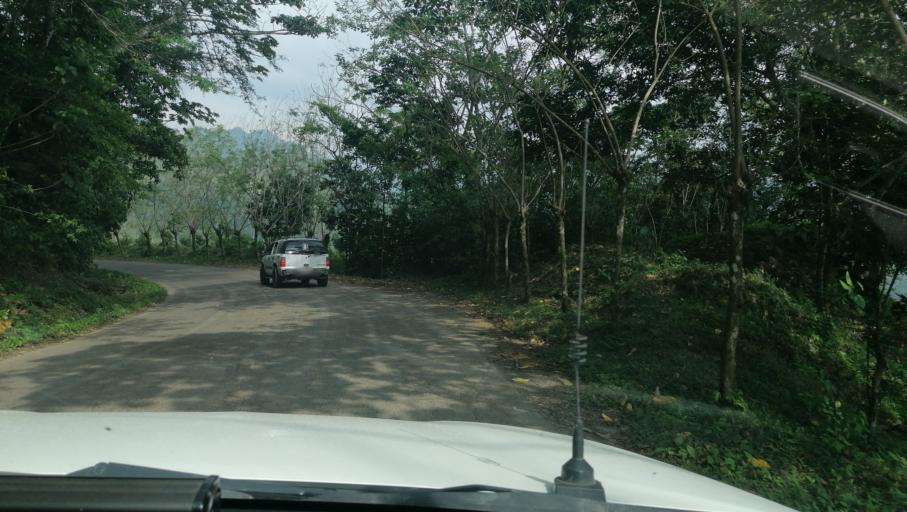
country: MX
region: Chiapas
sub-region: Francisco Leon
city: San Miguel la Sardina
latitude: 17.2273
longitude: -93.3465
